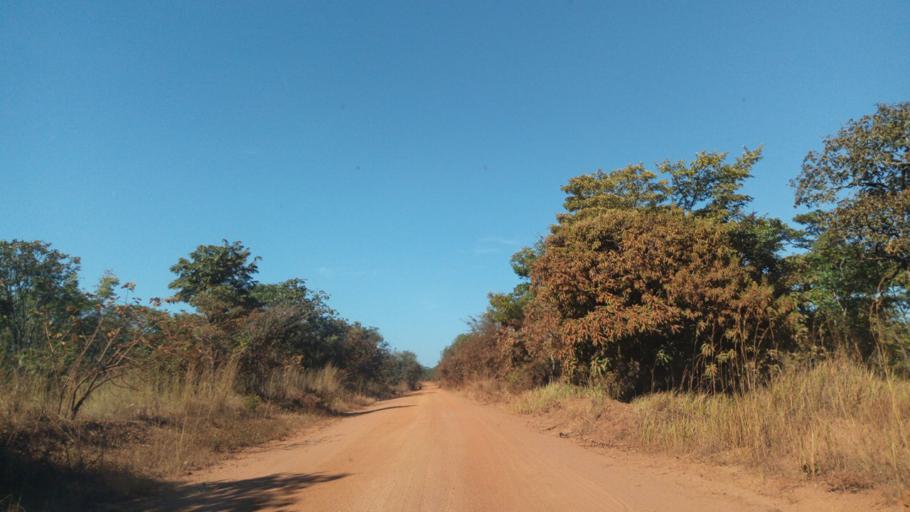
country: ZM
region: Luapula
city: Mwense
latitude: -10.6539
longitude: 28.4084
